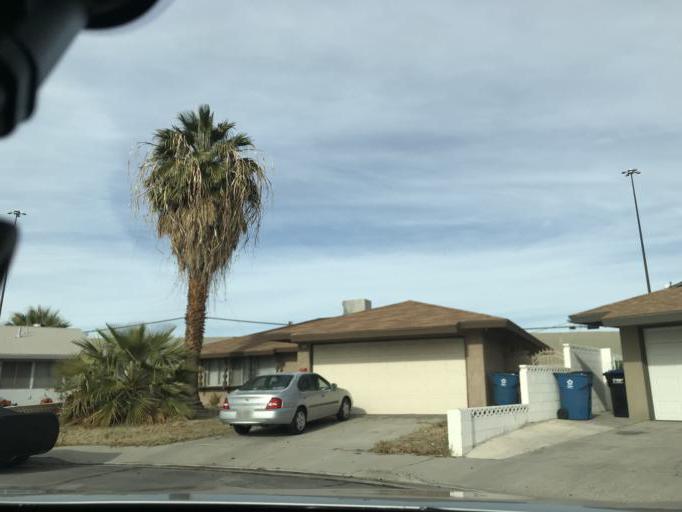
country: US
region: Nevada
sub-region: Clark County
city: Las Vegas
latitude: 36.1751
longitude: -115.1651
